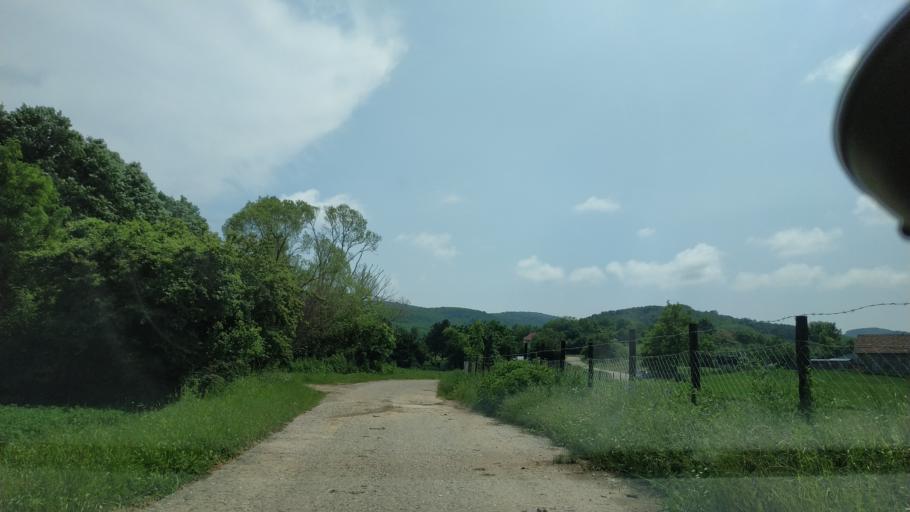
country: RS
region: Central Serbia
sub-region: Nisavski Okrug
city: Aleksinac
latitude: 43.4202
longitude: 21.7175
